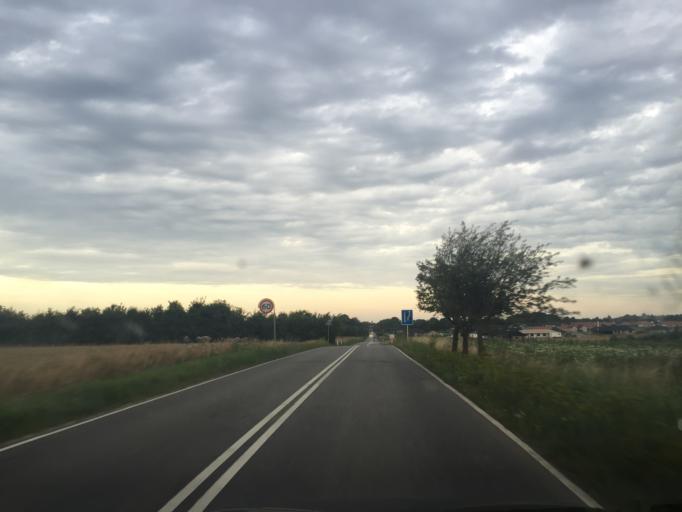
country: DK
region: Zealand
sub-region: Roskilde Kommune
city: Gundsomagle
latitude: 55.7328
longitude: 12.1718
